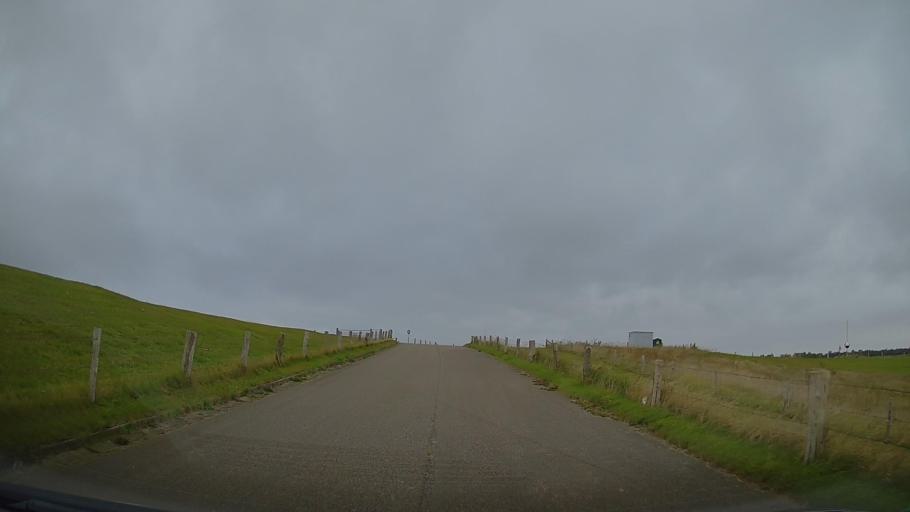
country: DE
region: Schleswig-Holstein
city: Busenwurth
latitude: 54.0684
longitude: 8.9820
